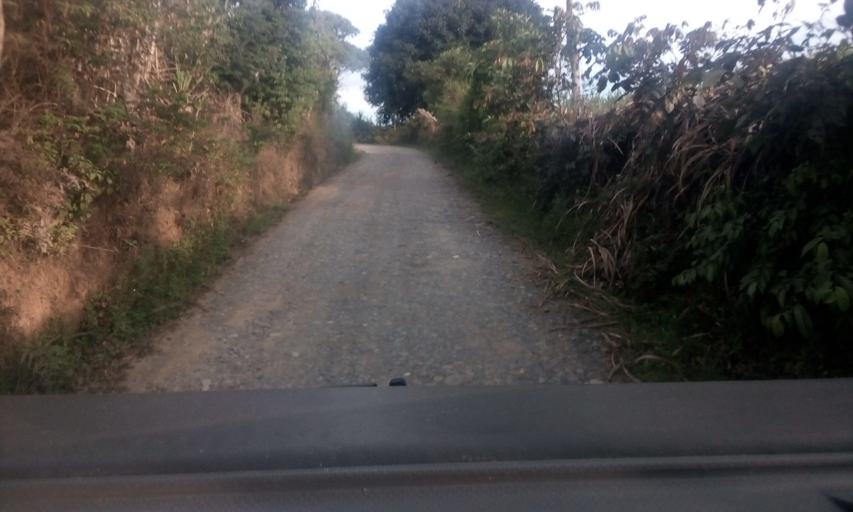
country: CO
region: Boyaca
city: Santana
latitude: 6.0225
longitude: -73.5156
